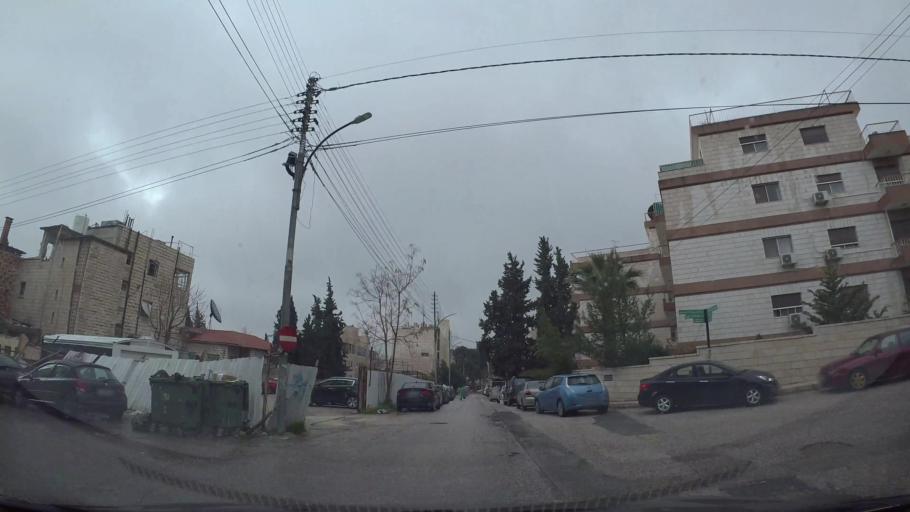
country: JO
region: Amman
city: Amman
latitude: 31.9513
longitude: 35.9051
